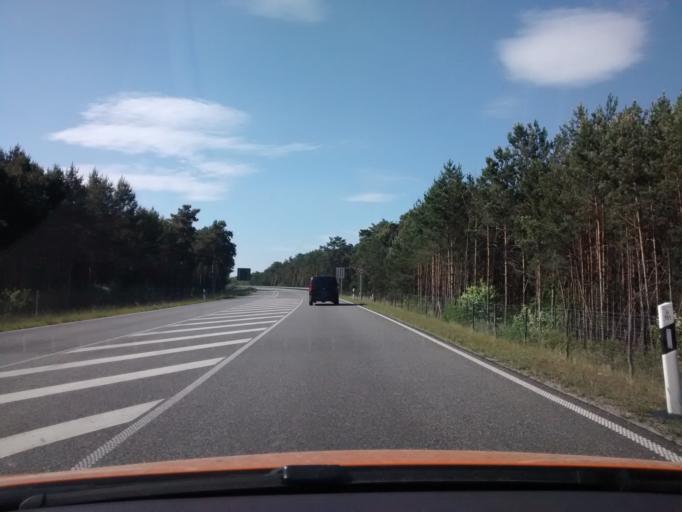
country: DE
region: Brandenburg
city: Luckenwalde
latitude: 52.0803
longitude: 13.1311
